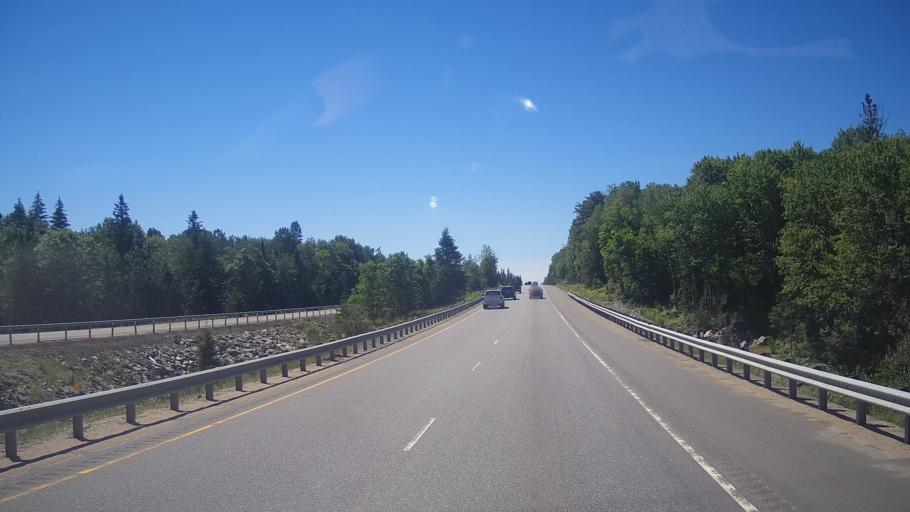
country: CA
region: Ontario
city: Bracebridge
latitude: 45.1413
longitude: -79.3115
